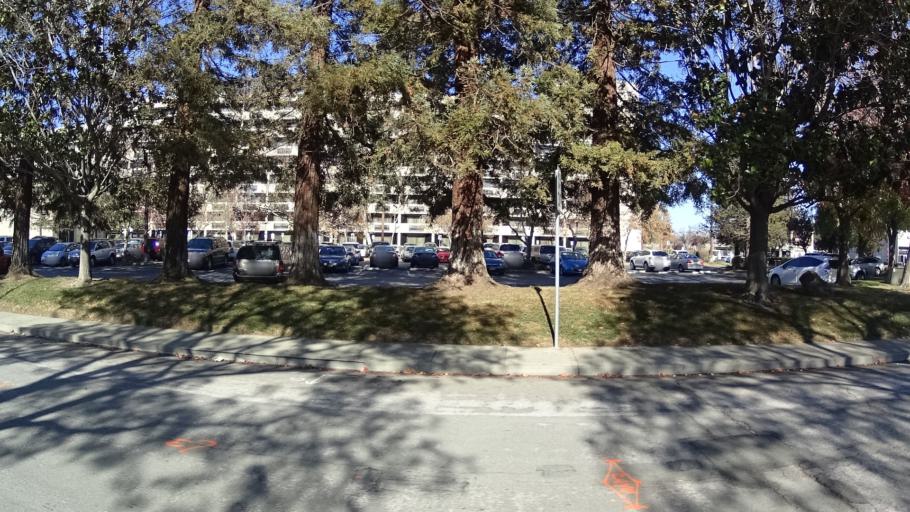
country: US
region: California
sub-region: Santa Clara County
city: Santa Clara
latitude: 37.3707
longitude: -121.9218
